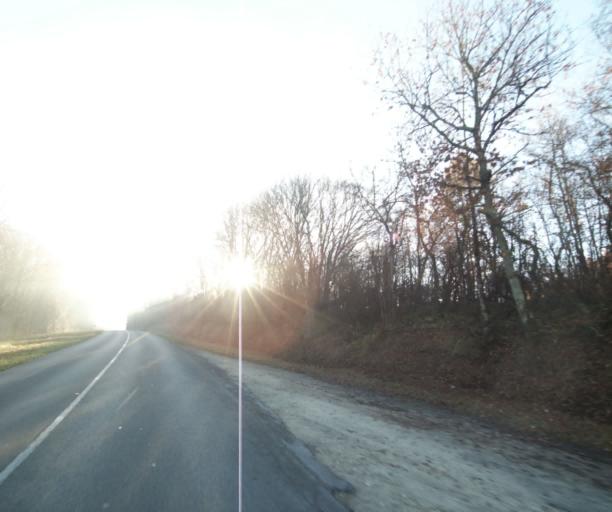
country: FR
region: Poitou-Charentes
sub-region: Departement de la Charente-Maritime
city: Bussac-sur-Charente
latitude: 45.7755
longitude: -0.6236
